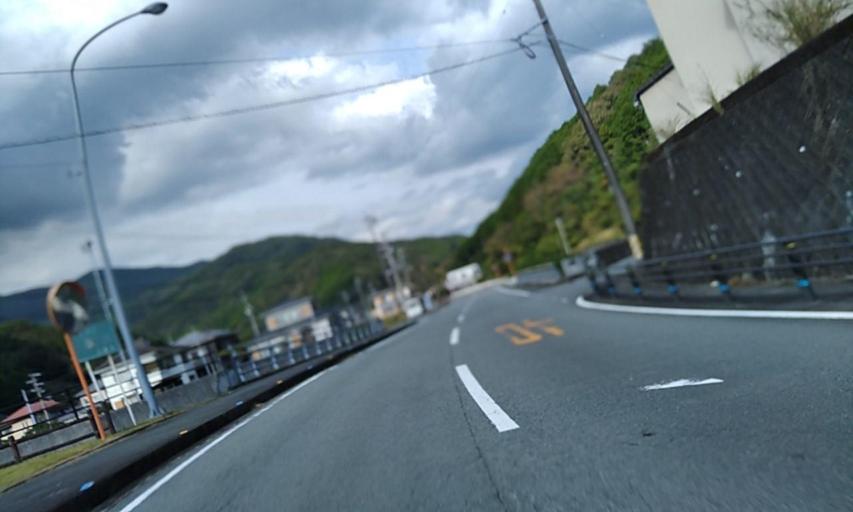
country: JP
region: Mie
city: Owase
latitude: 34.2252
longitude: 136.3940
